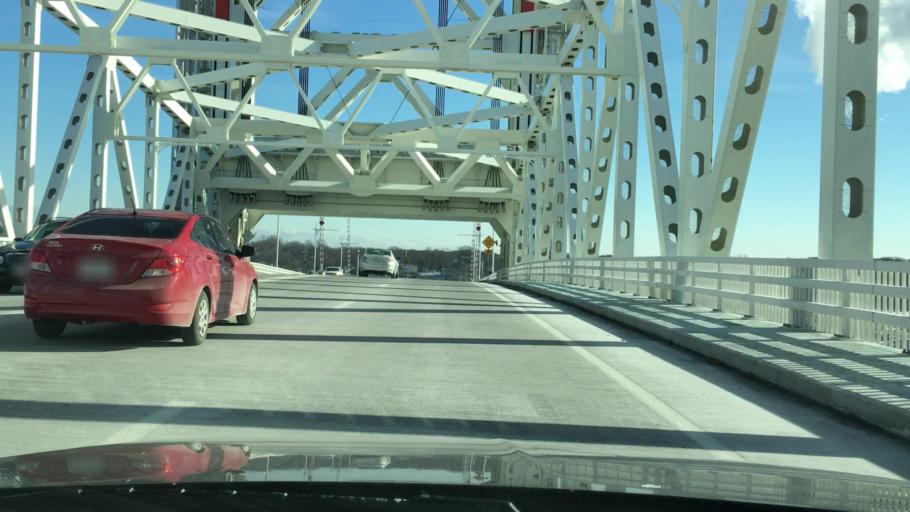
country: US
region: Massachusetts
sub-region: Norfolk County
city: Quincy
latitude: 42.2446
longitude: -70.9673
